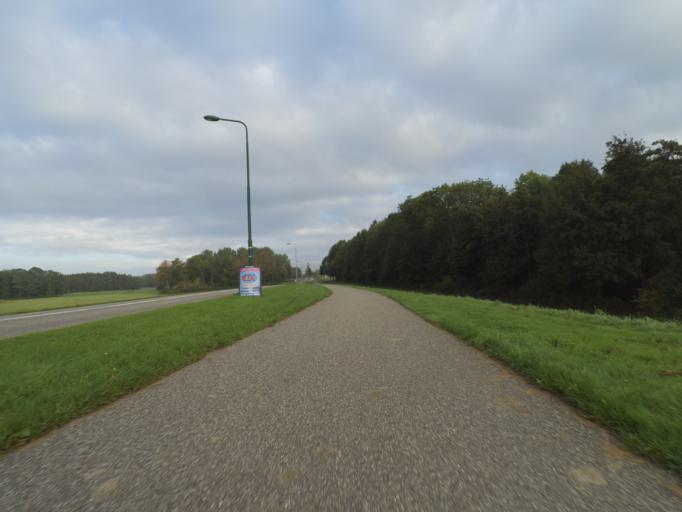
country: NL
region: Flevoland
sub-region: Gemeente Dronten
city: Dronten
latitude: 52.5250
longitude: 5.6959
